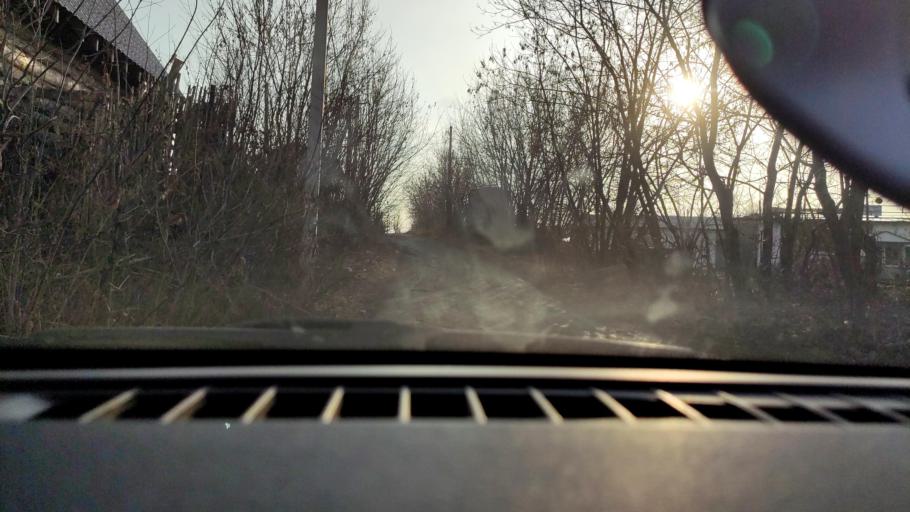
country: RU
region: Perm
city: Kondratovo
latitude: 57.9570
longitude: 56.1527
